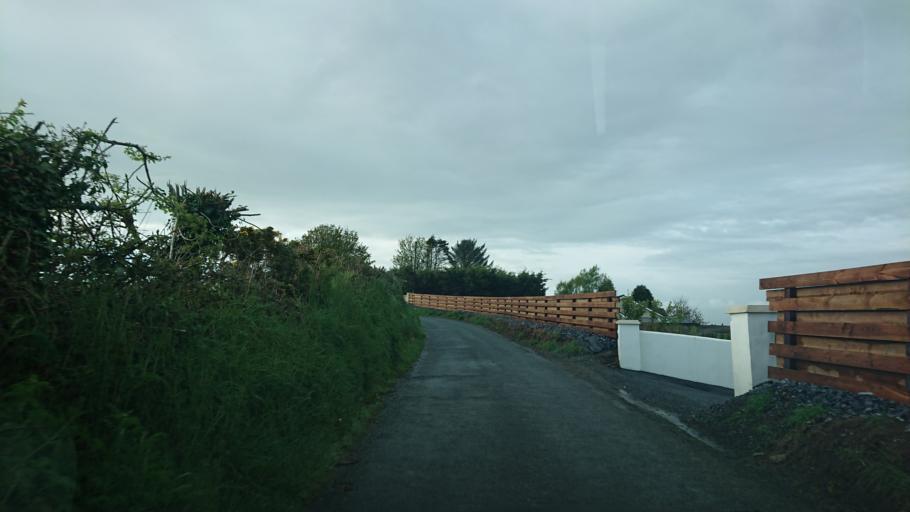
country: IE
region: Munster
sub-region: Waterford
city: Waterford
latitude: 52.2223
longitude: -7.1312
